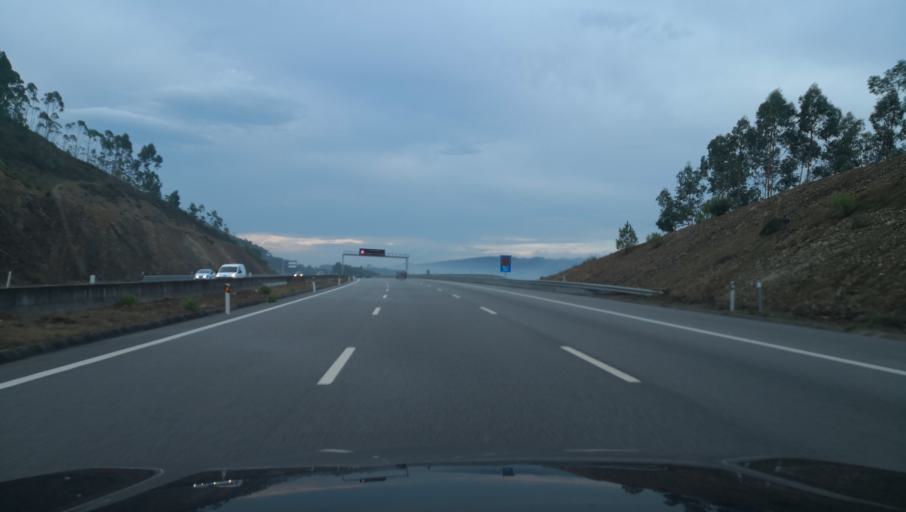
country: PT
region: Porto
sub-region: Paredes
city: Recarei
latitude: 41.1199
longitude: -8.4335
